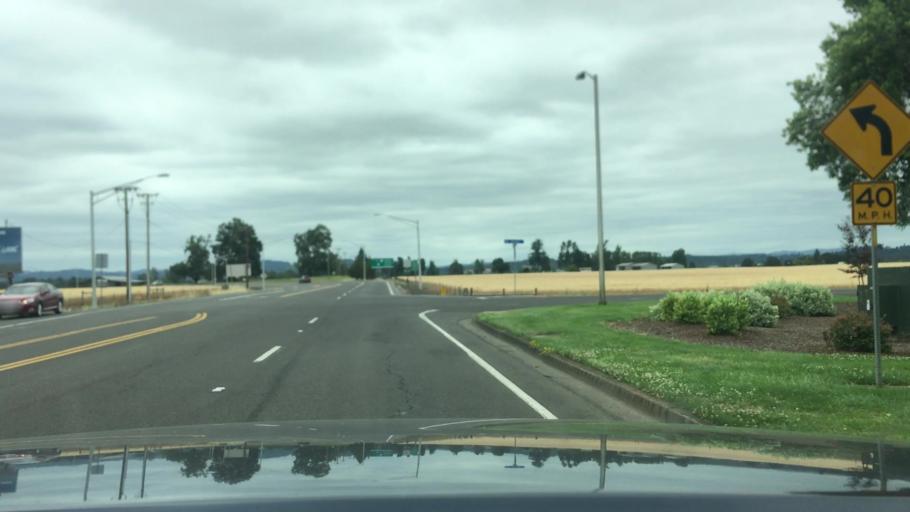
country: US
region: Oregon
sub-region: Lane County
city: Junction City
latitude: 44.1139
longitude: -123.2085
